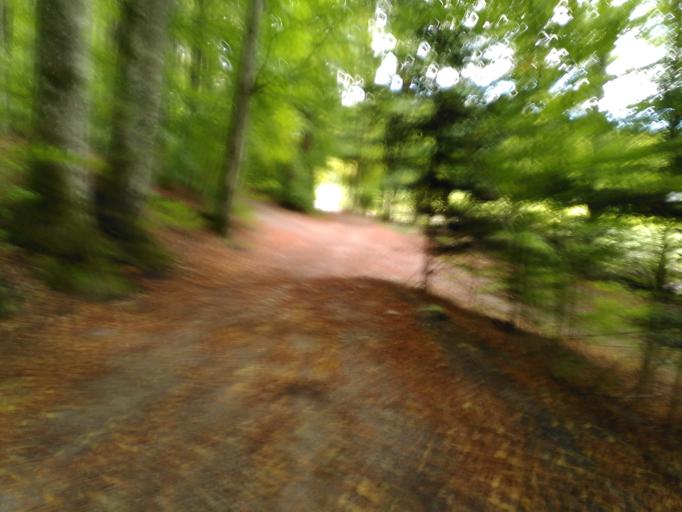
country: CH
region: Bern
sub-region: Emmental District
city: Ersigen
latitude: 47.0923
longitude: 7.6114
